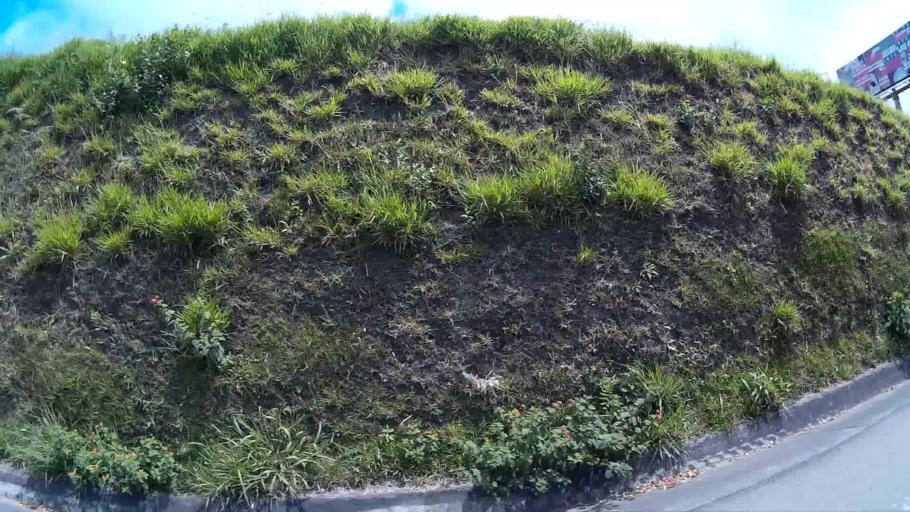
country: CO
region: Quindio
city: Circasia
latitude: 4.6211
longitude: -75.6261
